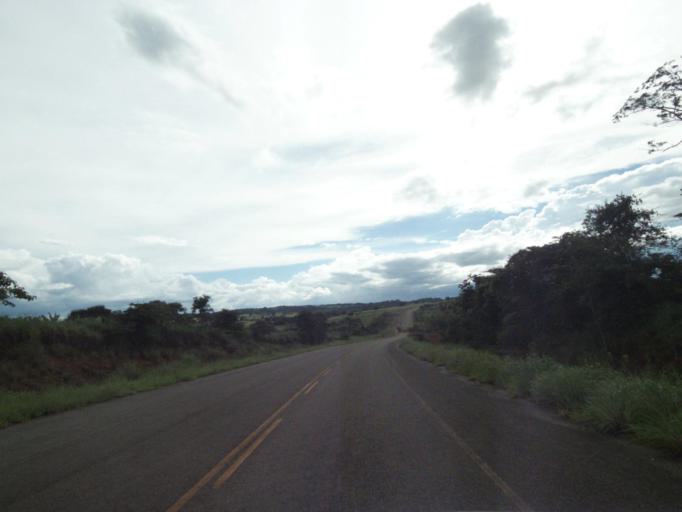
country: BR
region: Goias
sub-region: Jaragua
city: Jaragua
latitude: -15.8780
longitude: -49.4241
